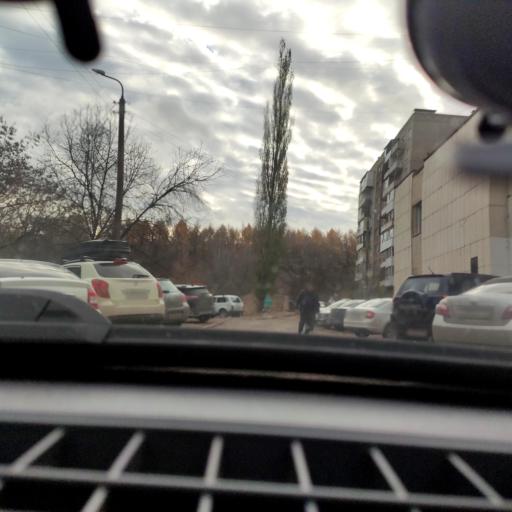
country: RU
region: Bashkortostan
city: Ufa
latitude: 54.7917
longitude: 56.0471
